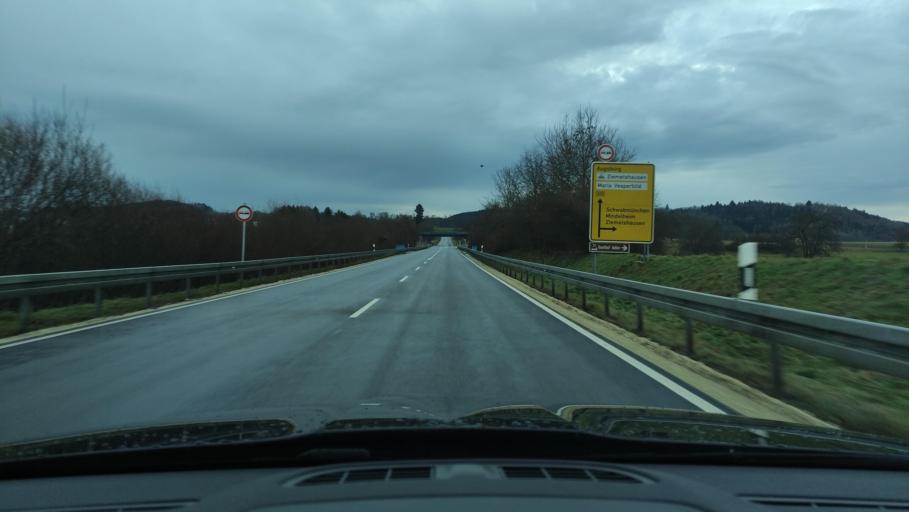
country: DE
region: Bavaria
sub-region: Swabia
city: Ziemetshausen
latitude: 48.2848
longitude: 10.5229
